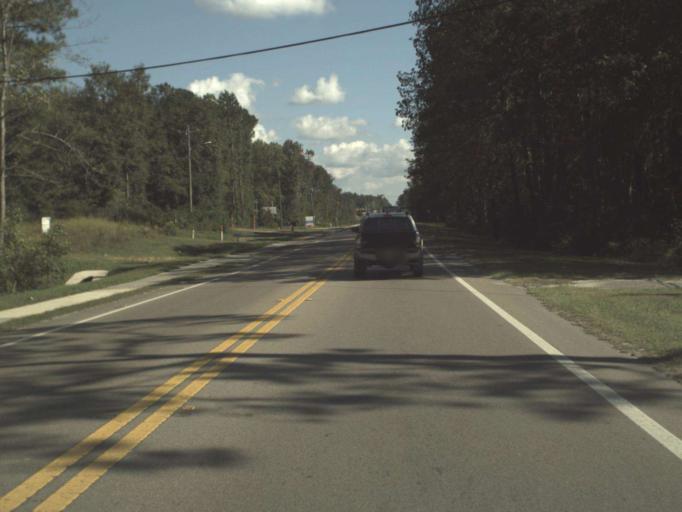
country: US
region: Florida
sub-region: Walton County
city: Freeport
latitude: 30.4957
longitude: -86.1311
